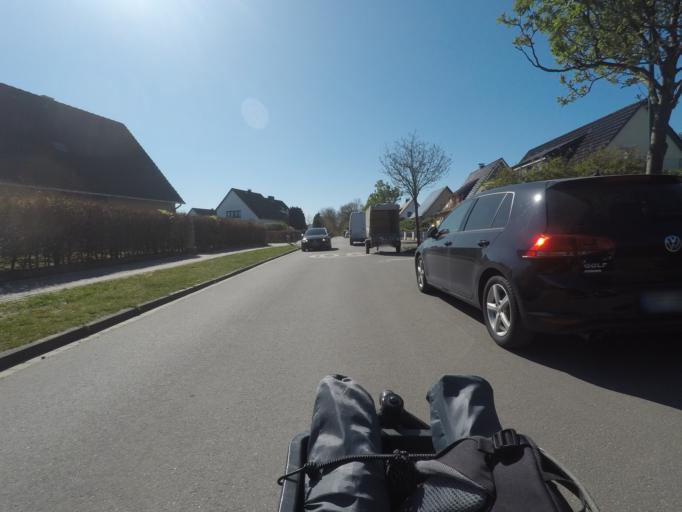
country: DE
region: Schleswig-Holstein
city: Stapelfeld
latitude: 53.6027
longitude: 10.2114
